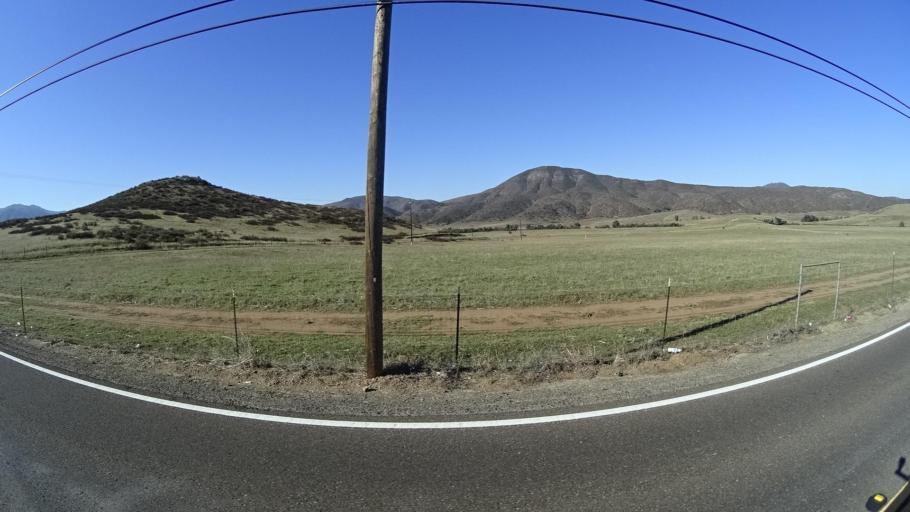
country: US
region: California
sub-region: San Diego County
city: Jamul
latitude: 32.6903
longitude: -116.8542
